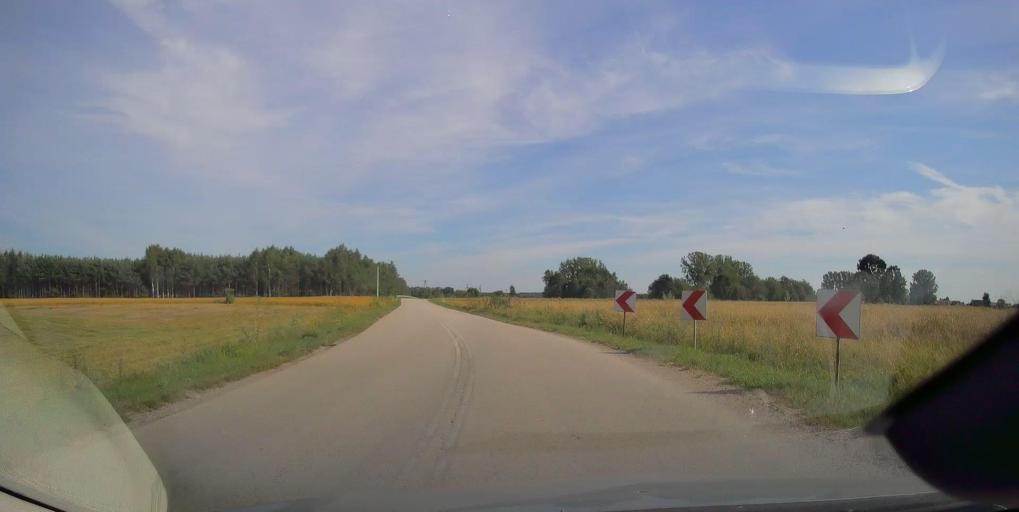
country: PL
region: Lodz Voivodeship
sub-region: Powiat opoczynski
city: Mniszkow
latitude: 51.3549
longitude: 20.0373
